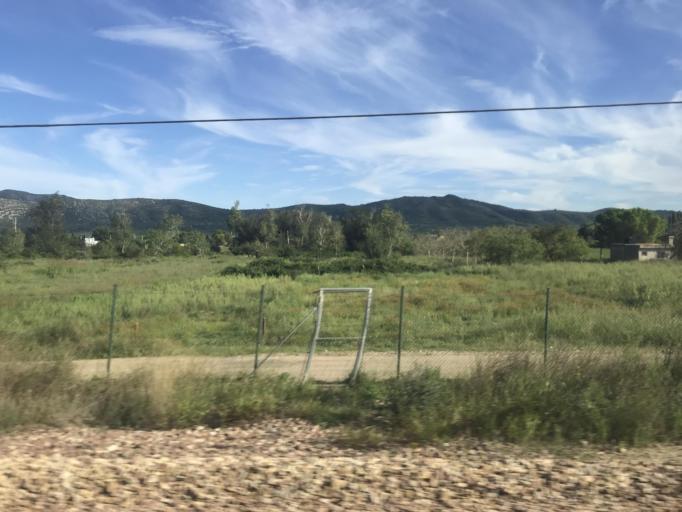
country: ES
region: Catalonia
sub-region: Provincia de Tarragona
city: Ulldecona
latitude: 40.6020
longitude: 0.4563
